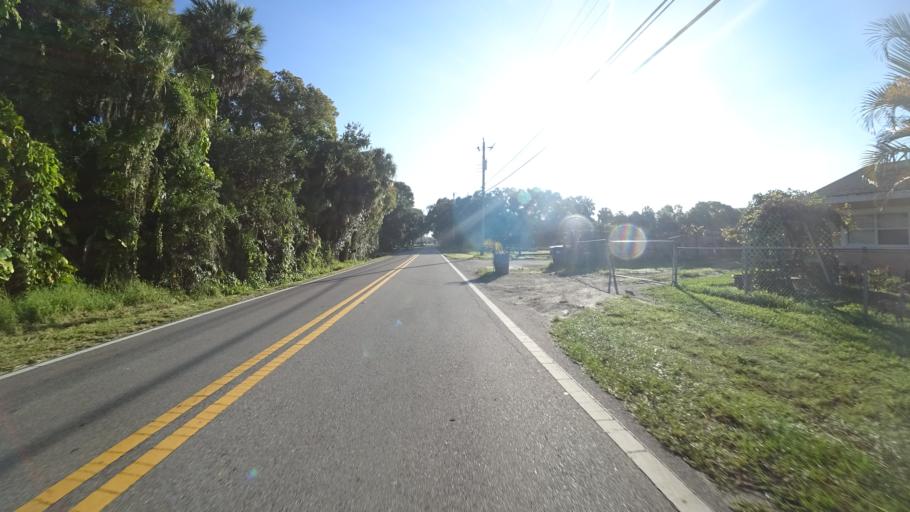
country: US
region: Florida
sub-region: Manatee County
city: Memphis
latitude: 27.5579
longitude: -82.5442
